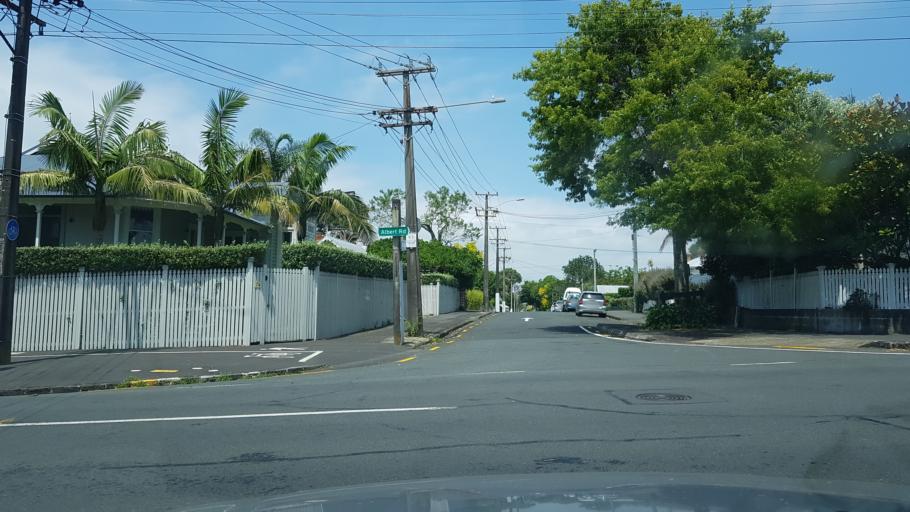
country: NZ
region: Auckland
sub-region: Auckland
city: Auckland
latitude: -36.8241
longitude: 174.8003
